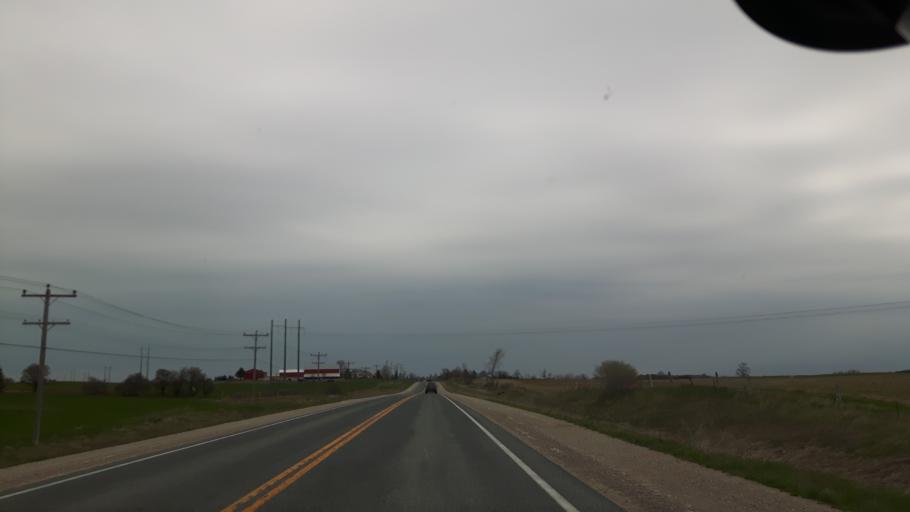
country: CA
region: Ontario
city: Goderich
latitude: 43.6736
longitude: -81.6246
